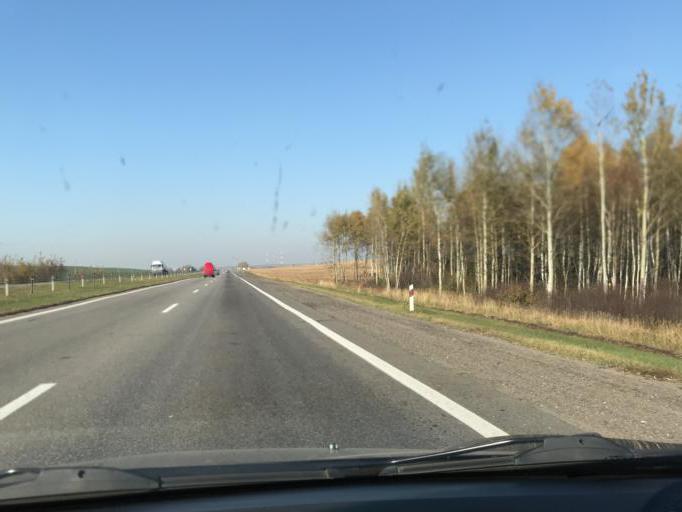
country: BY
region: Minsk
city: Luhavaya Slabada
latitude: 53.7199
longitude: 27.8638
